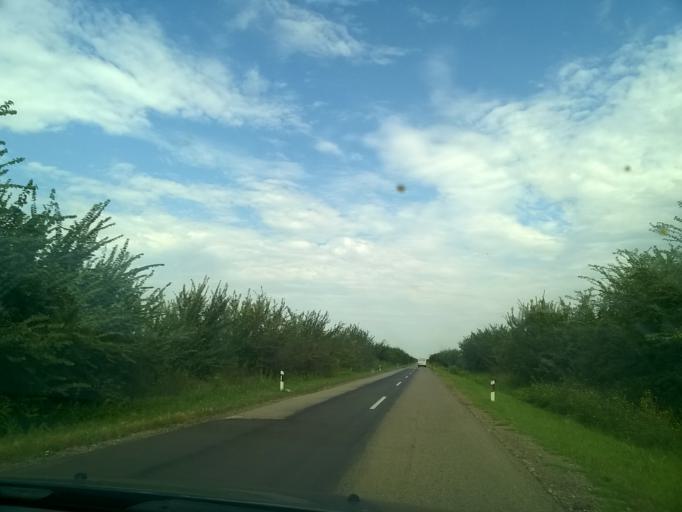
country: RS
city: Stajicevo
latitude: 45.2938
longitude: 20.5013
